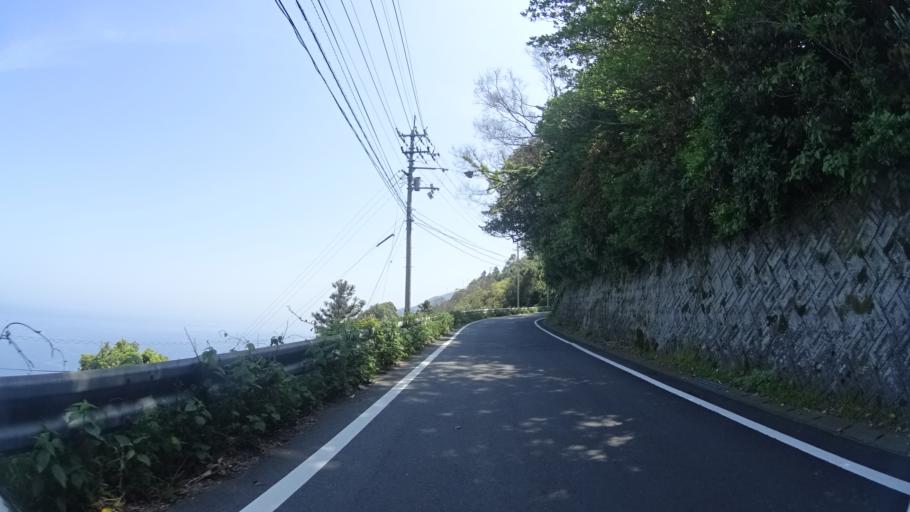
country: JP
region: Ehime
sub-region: Nishiuwa-gun
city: Ikata-cho
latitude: 33.3795
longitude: 132.0669
